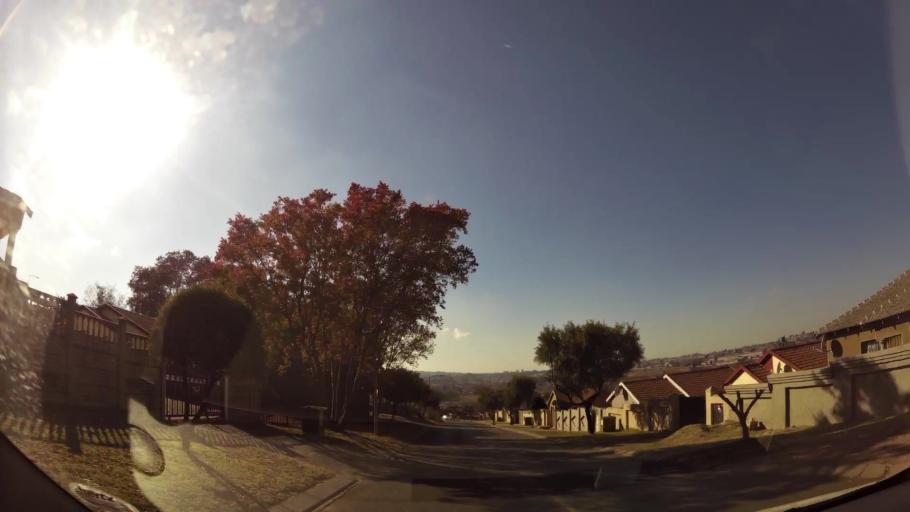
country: ZA
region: Gauteng
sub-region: City of Johannesburg Metropolitan Municipality
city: Roodepoort
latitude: -26.1560
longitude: 27.8342
